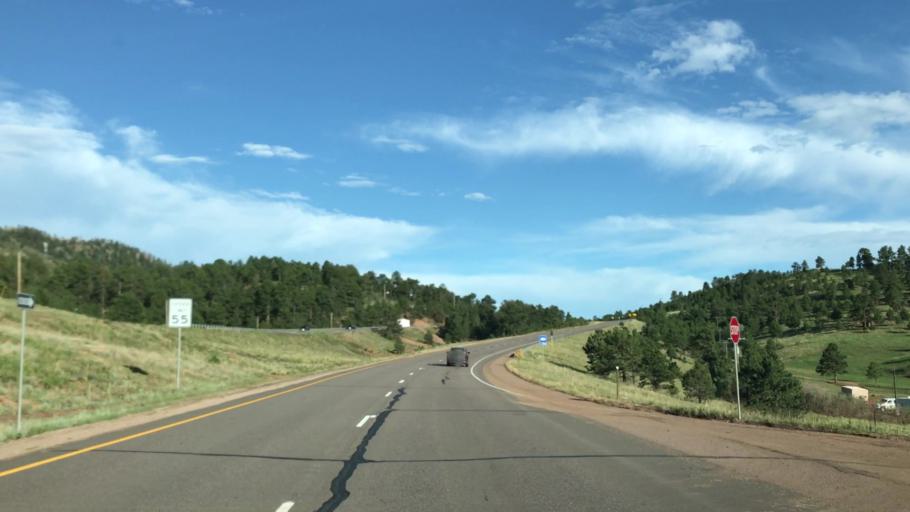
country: US
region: Colorado
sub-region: El Paso County
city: Cascade-Chipita Park
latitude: 38.9397
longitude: -105.0131
